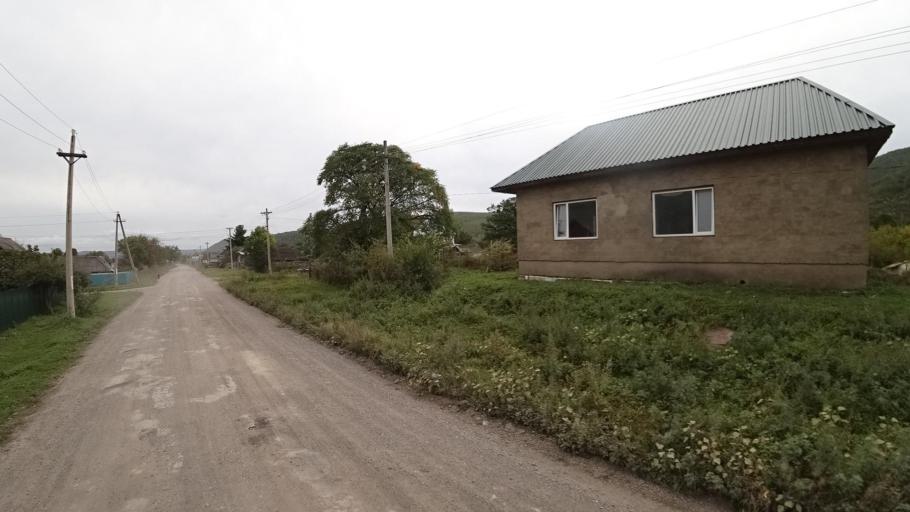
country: RU
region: Jewish Autonomous Oblast
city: Khingansk
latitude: 49.0357
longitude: 131.0495
